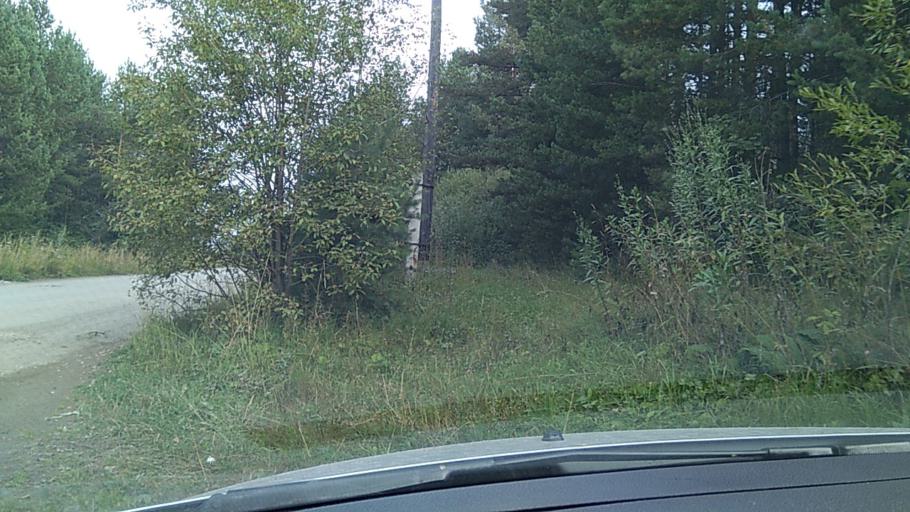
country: RU
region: Chelyabinsk
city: Zlatoust
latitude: 55.1626
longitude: 59.6985
